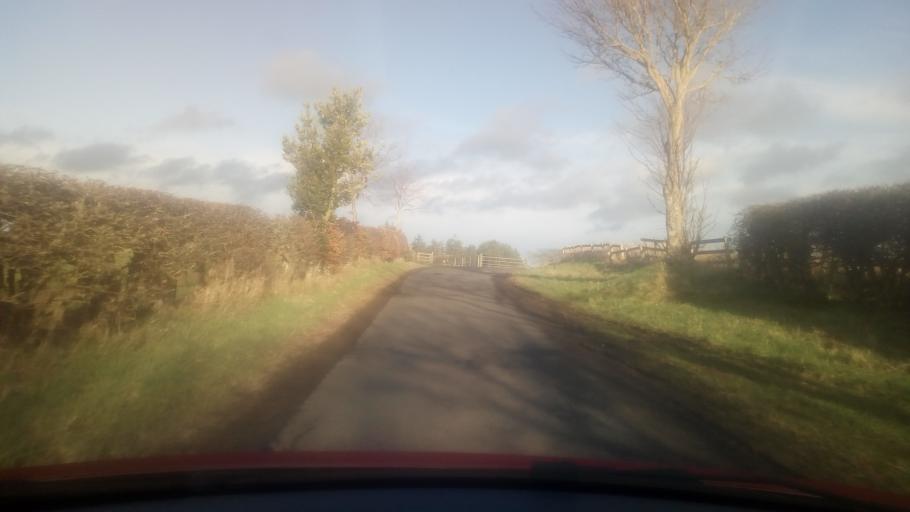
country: GB
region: Scotland
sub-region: The Scottish Borders
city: Duns
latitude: 55.7377
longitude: -2.3315
